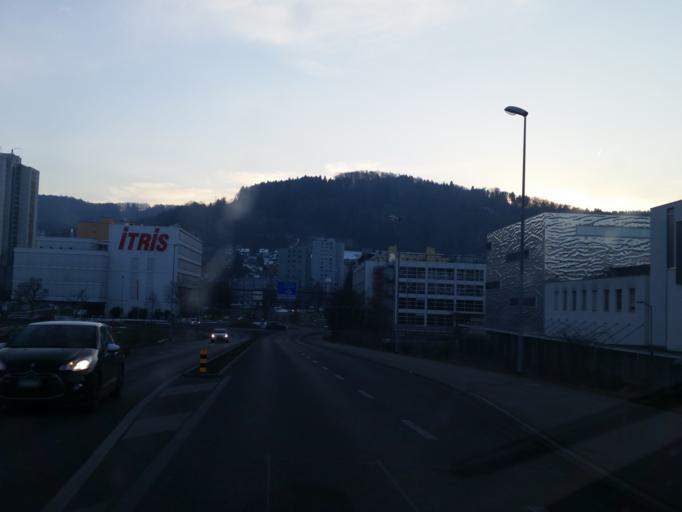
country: CH
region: Aargau
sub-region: Bezirk Baden
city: Spreitenbach
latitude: 47.4277
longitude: 8.3668
